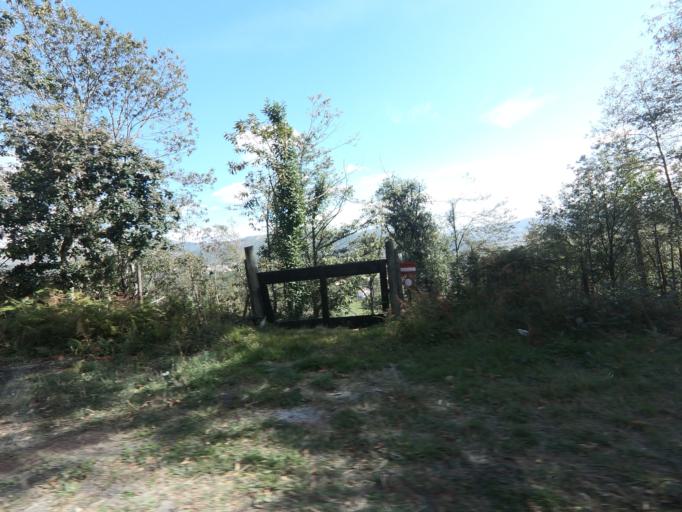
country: PT
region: Vila Real
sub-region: Santa Marta de Penaguiao
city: Santa Marta de Penaguiao
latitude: 41.3002
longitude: -7.8880
